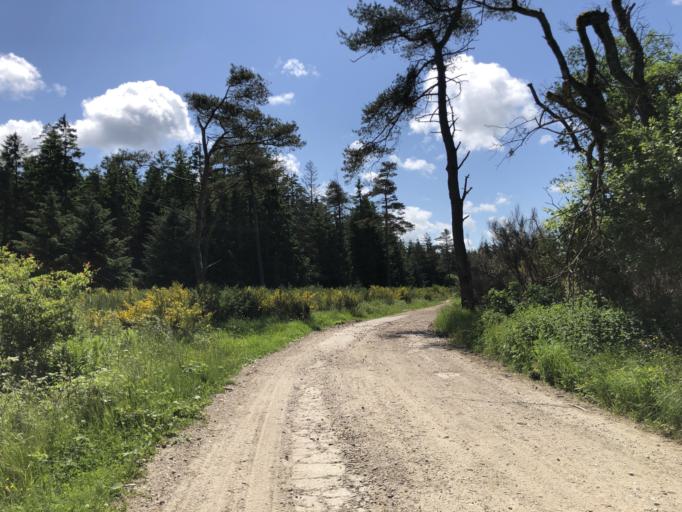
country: DK
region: Central Jutland
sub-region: Lemvig Kommune
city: Lemvig
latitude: 56.4962
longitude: 8.3318
